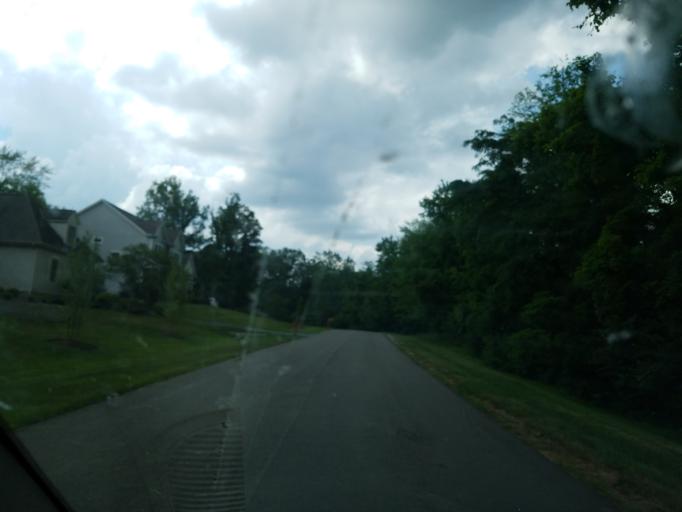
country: US
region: Ohio
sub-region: Delaware County
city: Powell
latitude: 40.1733
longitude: -83.0529
